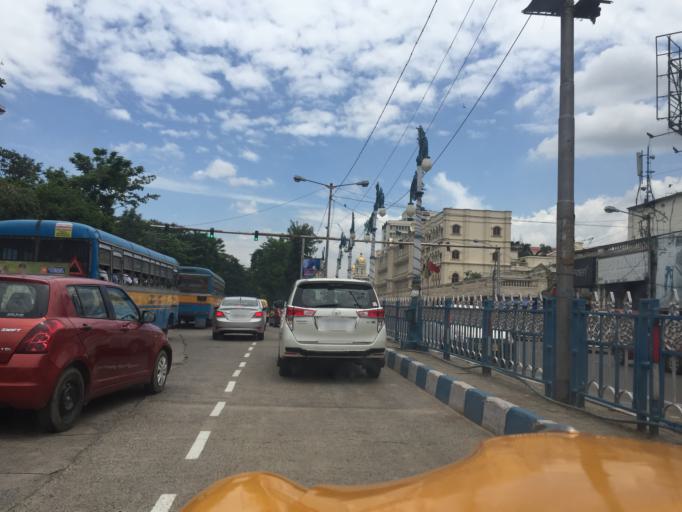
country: IN
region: West Bengal
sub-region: Kolkata
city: Bara Bazar
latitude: 22.5602
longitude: 88.3506
